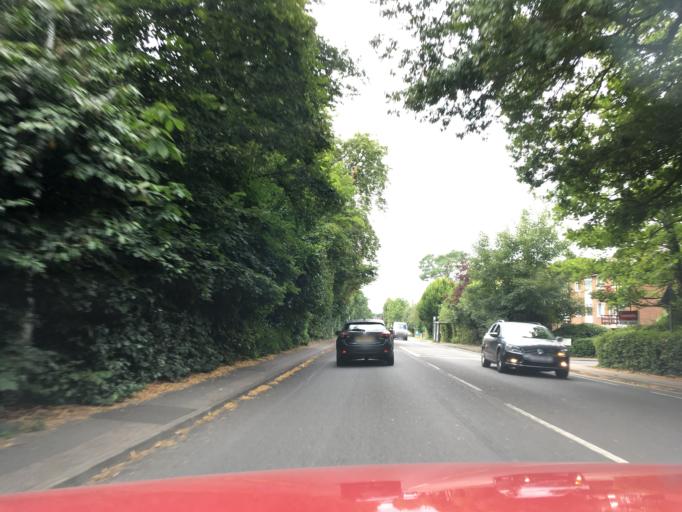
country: GB
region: England
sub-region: Surrey
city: Felbridge
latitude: 51.1340
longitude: -0.0255
